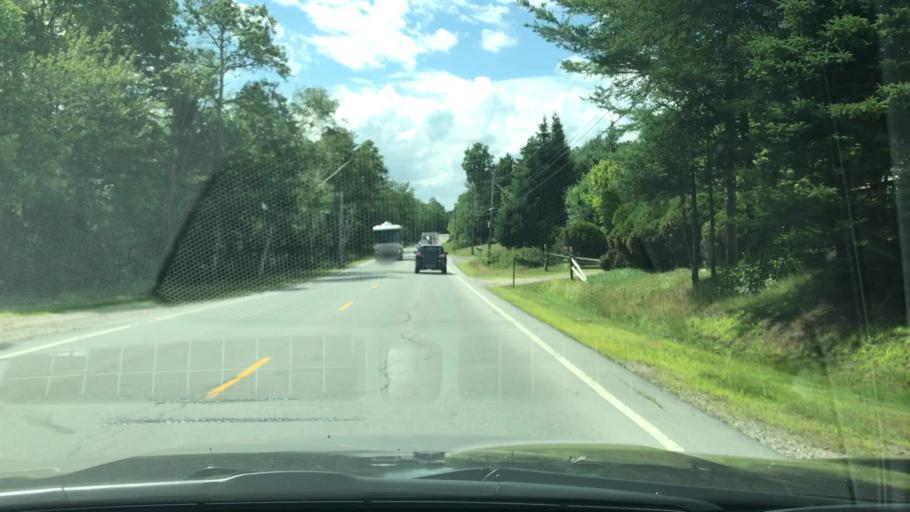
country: US
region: New Hampshire
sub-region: Coos County
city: Jefferson
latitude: 44.3599
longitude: -71.3706
